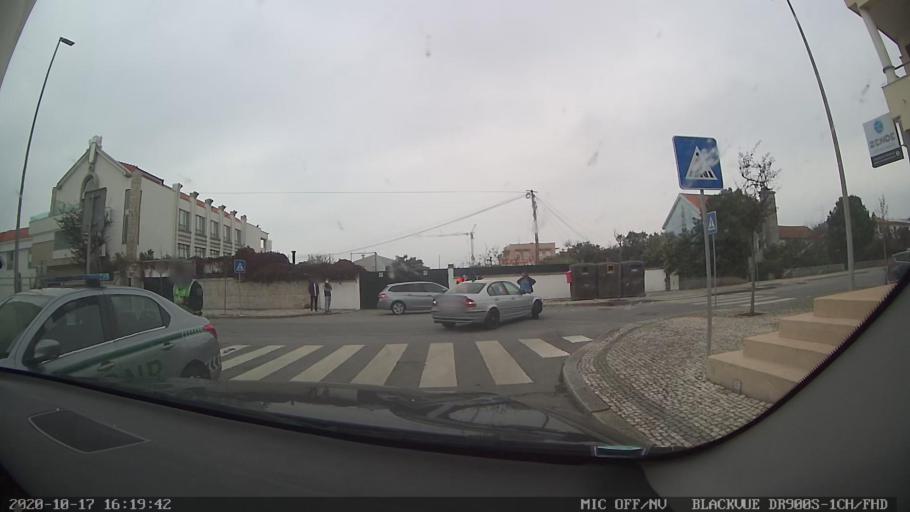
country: PT
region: Braga
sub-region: Esposende
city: Esposende
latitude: 41.5404
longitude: -8.7853
